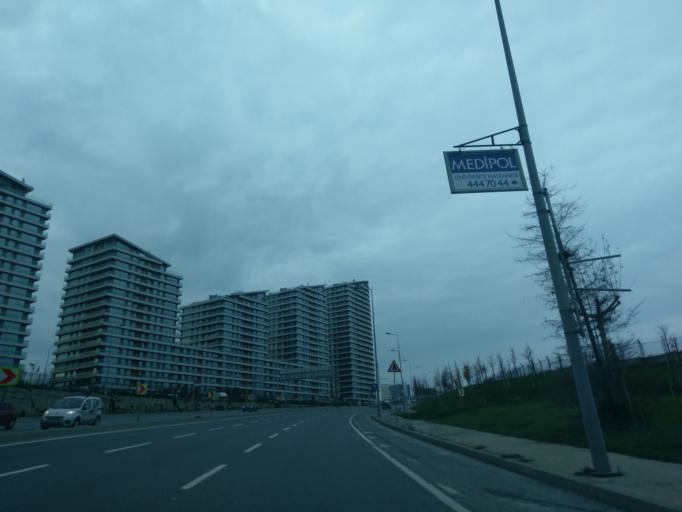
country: TR
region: Istanbul
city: Mahmutbey
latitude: 41.0651
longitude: 28.8430
